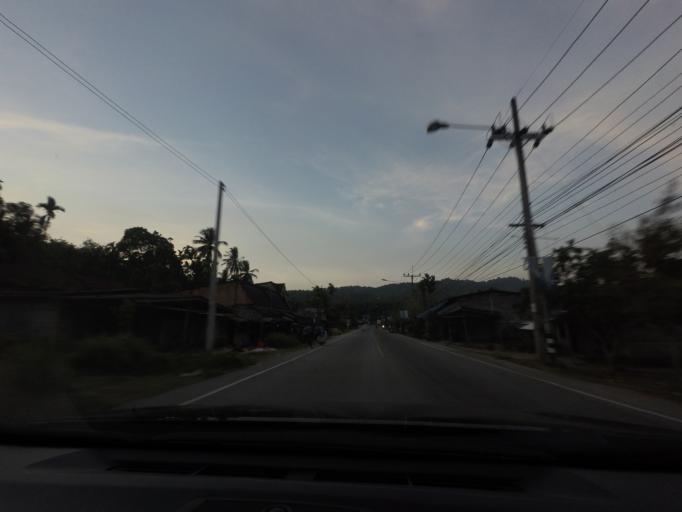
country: TH
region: Narathiwat
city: Rueso
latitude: 6.3711
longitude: 101.5562
